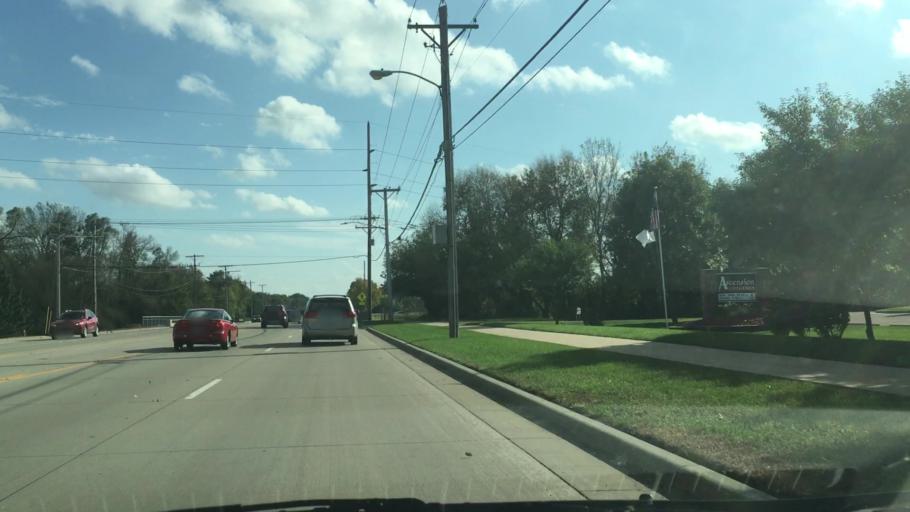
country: US
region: Minnesota
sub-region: Olmsted County
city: Rochester
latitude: 43.9914
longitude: -92.4425
